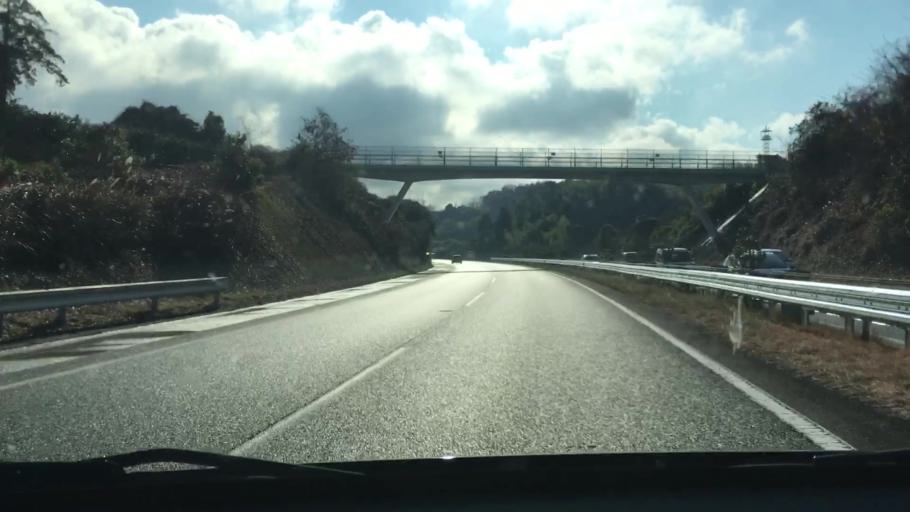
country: JP
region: Kumamoto
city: Matsubase
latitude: 32.5608
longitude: 130.6976
